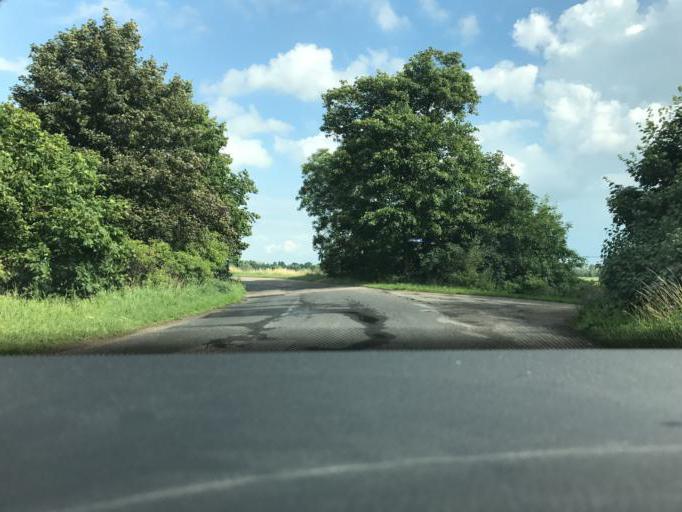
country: PL
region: Pomeranian Voivodeship
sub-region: Powiat gdanski
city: Cedry Wielkie
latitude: 54.3358
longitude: 18.8098
